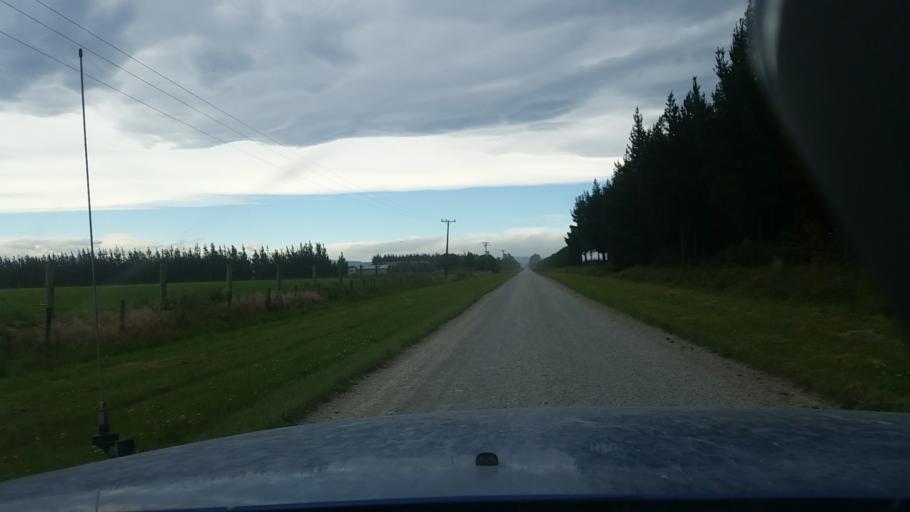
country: NZ
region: Canterbury
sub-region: Ashburton District
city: Tinwald
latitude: -43.9766
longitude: 171.6129
